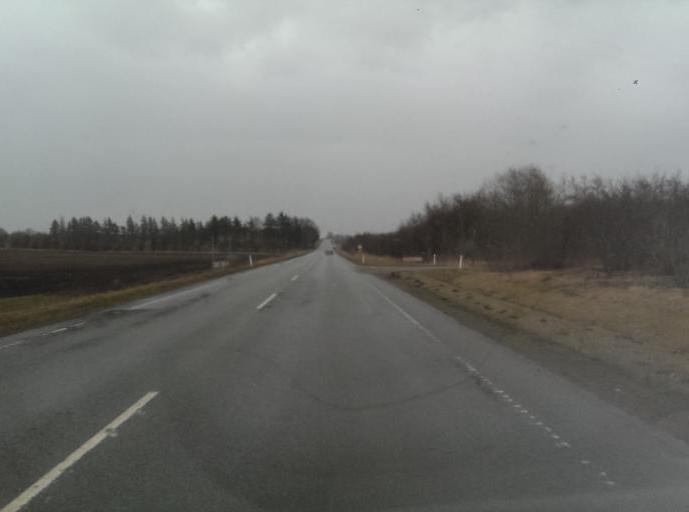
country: DK
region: Central Jutland
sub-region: Ringkobing-Skjern Kommune
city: Skjern
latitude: 56.0839
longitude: 8.4610
